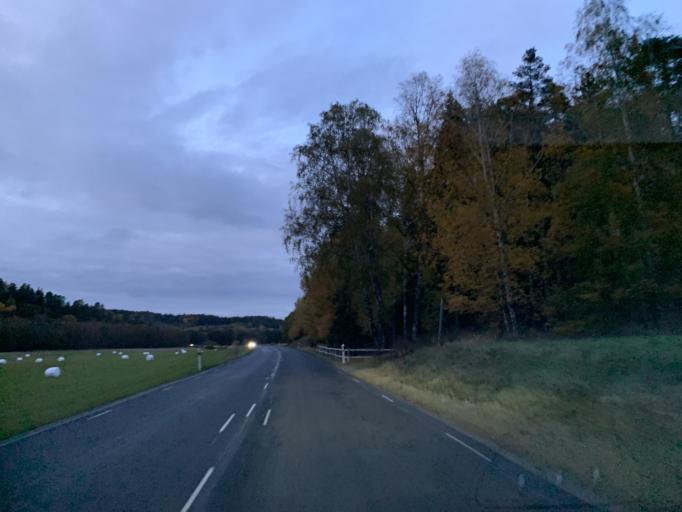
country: SE
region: Stockholm
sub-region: Botkyrka Kommun
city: Varsta
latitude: 59.1112
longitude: 17.8055
